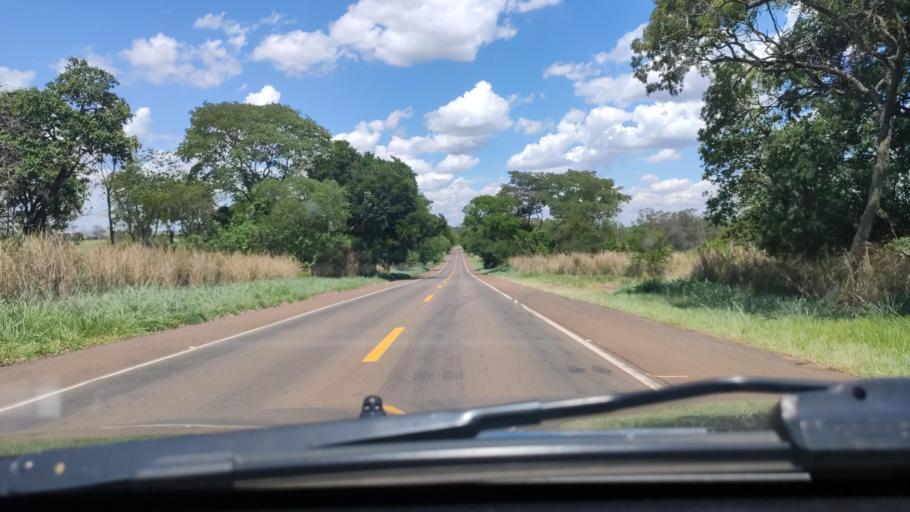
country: BR
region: Sao Paulo
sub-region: Boa Esperanca Do Sul
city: Boa Esperanca do Sul
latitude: -22.0696
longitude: -48.4148
